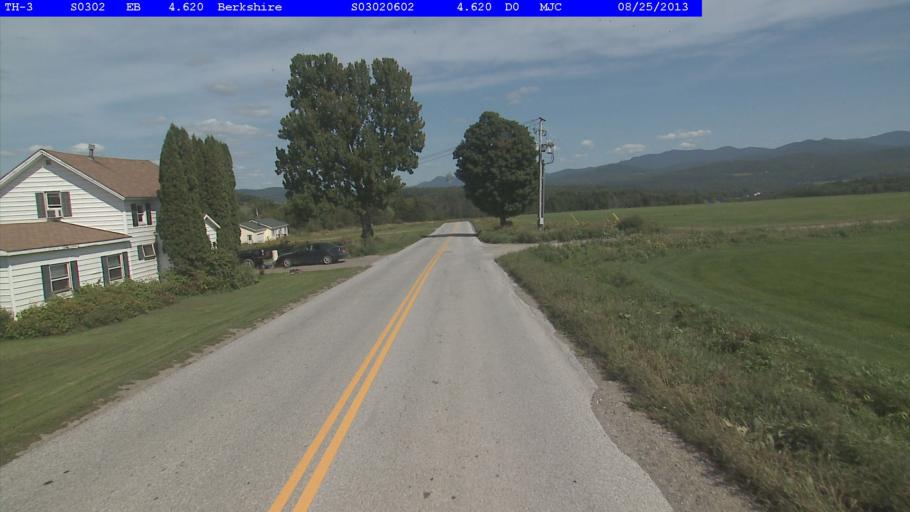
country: US
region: Vermont
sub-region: Franklin County
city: Richford
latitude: 44.9804
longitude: -72.7280
